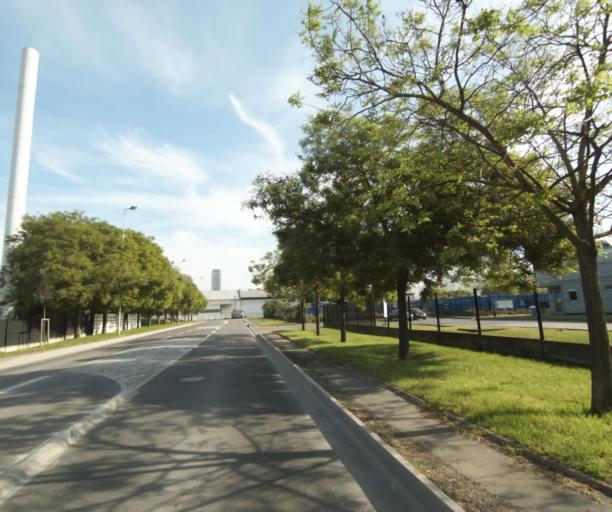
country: FR
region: Ile-de-France
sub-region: Departement des Hauts-de-Seine
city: Gennevilliers
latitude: 48.9482
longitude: 2.2956
